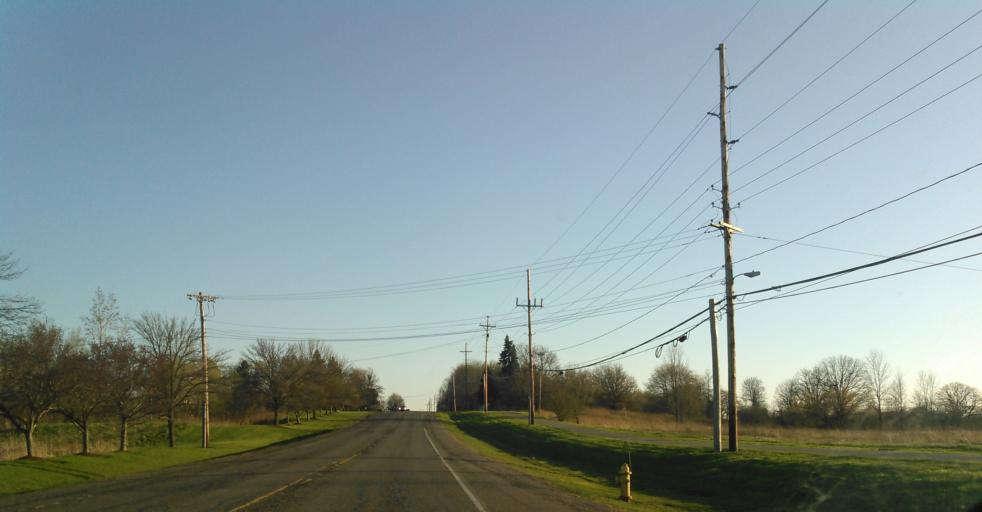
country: US
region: New York
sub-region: Monroe County
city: Rochester
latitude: 43.0774
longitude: -77.6622
